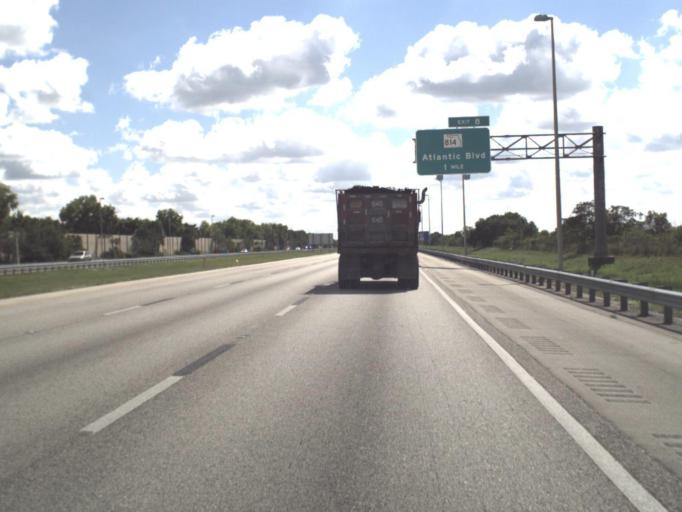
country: US
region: Florida
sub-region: Broward County
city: Coral Springs
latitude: 26.2539
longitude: -80.2974
